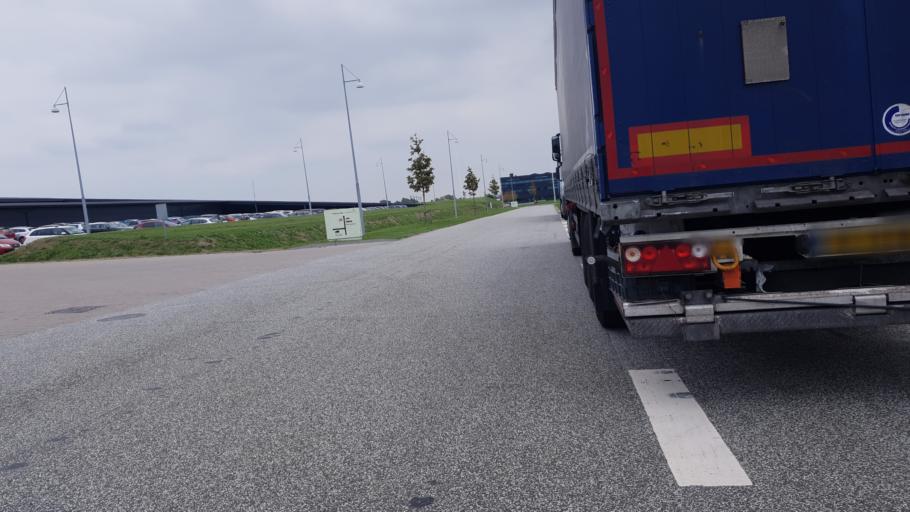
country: DK
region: South Denmark
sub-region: Middelfart Kommune
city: Strib
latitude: 55.5015
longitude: 9.7821
